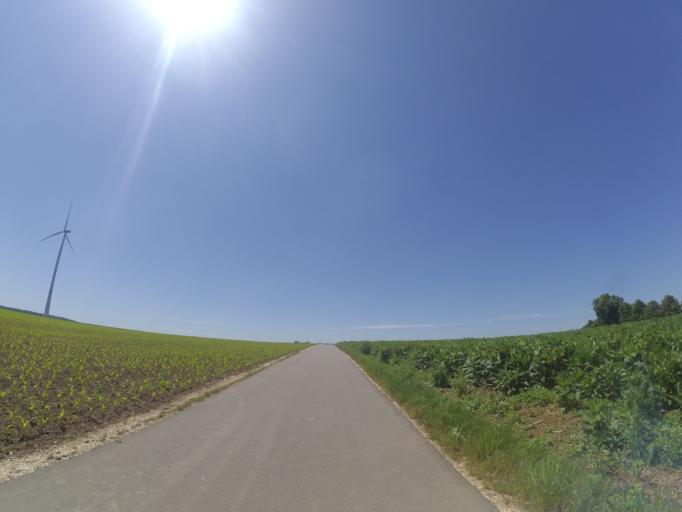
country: DE
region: Baden-Wuerttemberg
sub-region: Tuebingen Region
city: Berghulen
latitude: 48.4733
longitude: 9.8512
